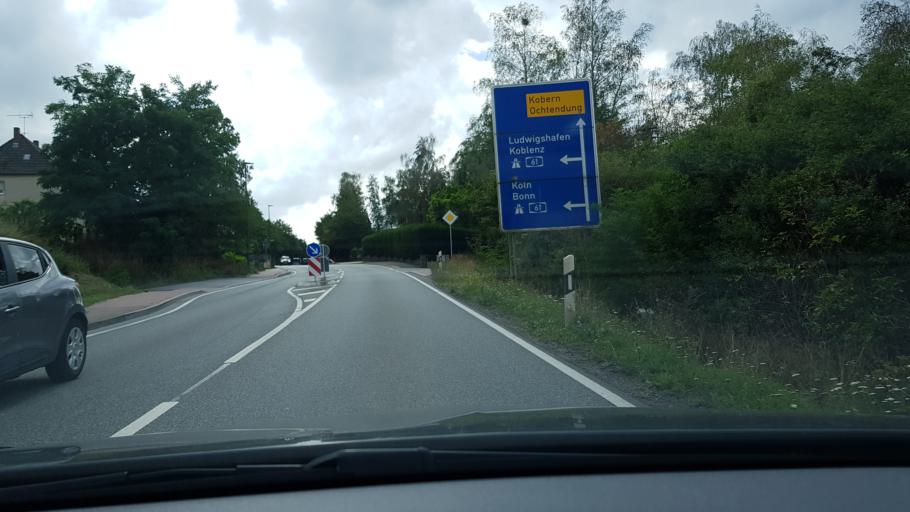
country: DE
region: Rheinland-Pfalz
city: Plaidt
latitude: 50.3827
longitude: 7.3871
